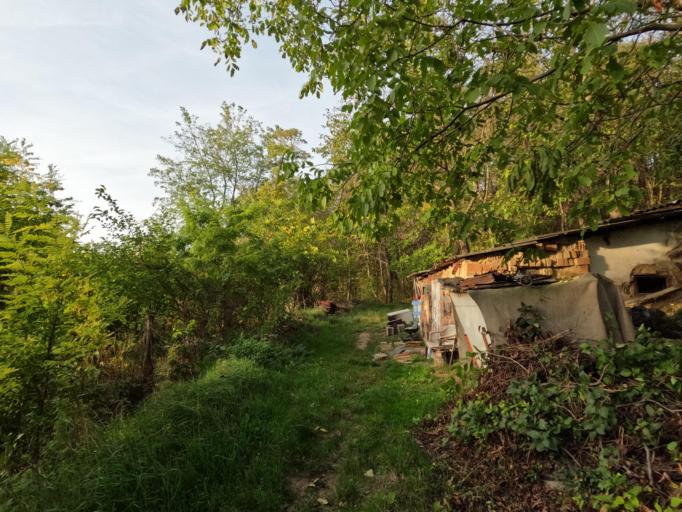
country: HU
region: Tolna
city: Szekszard
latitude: 46.3414
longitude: 18.6727
